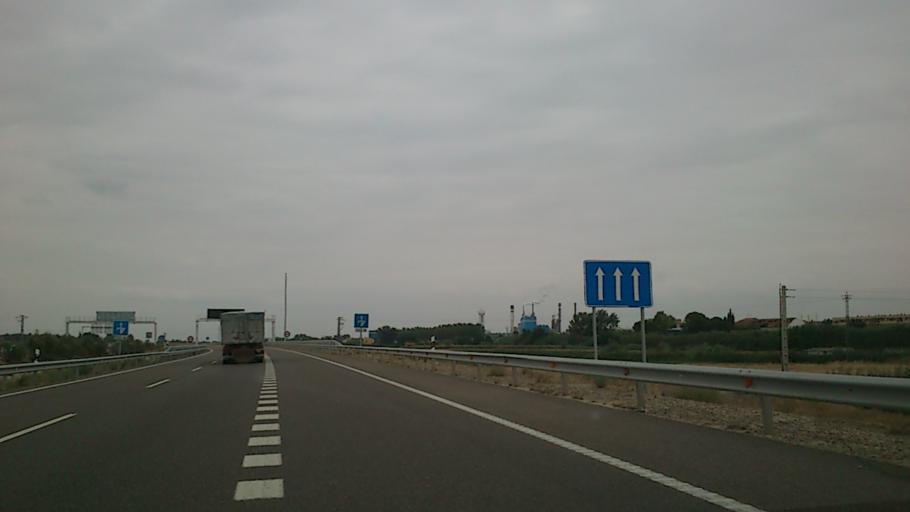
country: ES
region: Aragon
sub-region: Provincia de Zaragoza
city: Zaragoza
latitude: 41.6829
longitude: -0.8333
